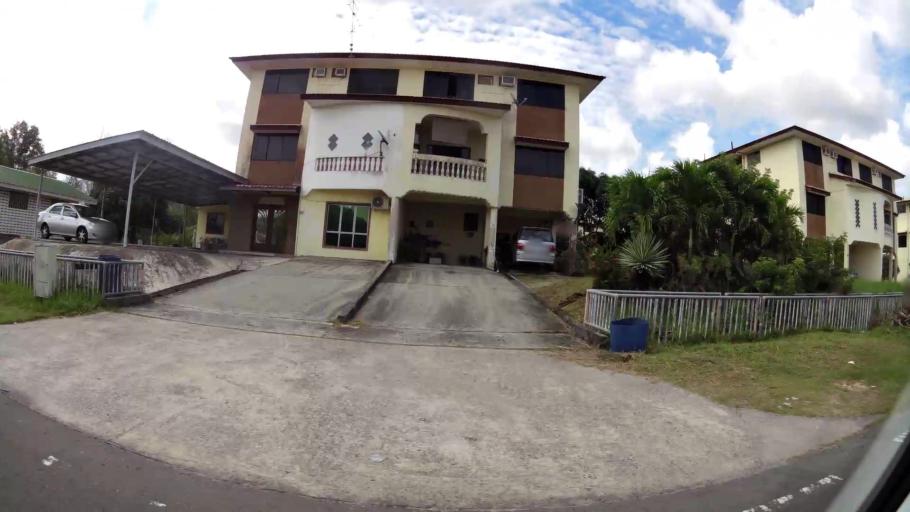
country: BN
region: Brunei and Muara
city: Bandar Seri Begawan
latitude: 4.9317
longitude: 114.8962
